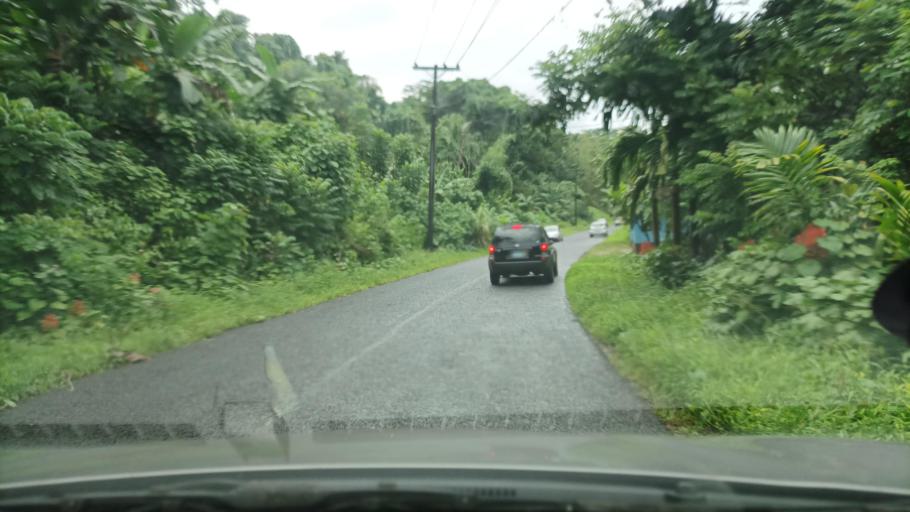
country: FM
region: Pohnpei
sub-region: Sokehs Municipality
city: Palikir - National Government Center
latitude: 6.8902
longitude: 158.1543
